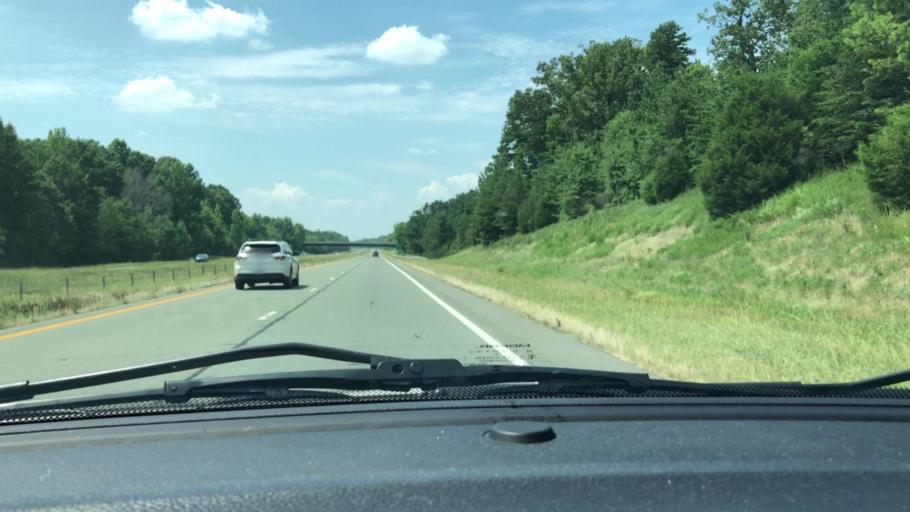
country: US
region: North Carolina
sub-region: Randolph County
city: Liberty
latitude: 35.7993
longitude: -79.5364
